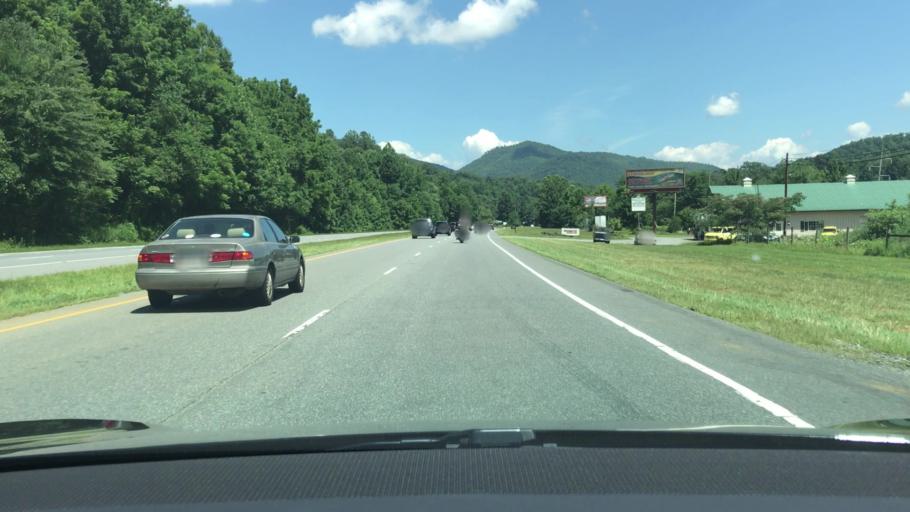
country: US
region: North Carolina
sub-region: Jackson County
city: Sylva
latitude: 35.3124
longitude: -83.2605
